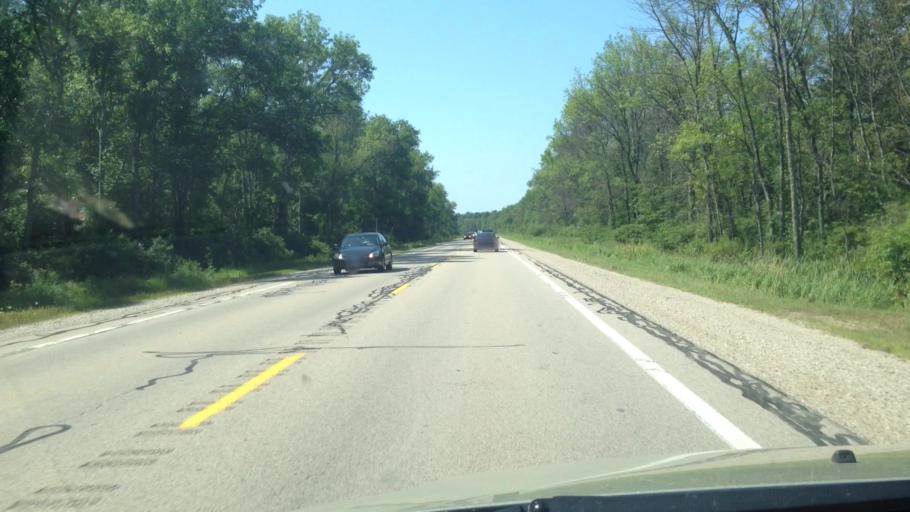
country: US
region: Michigan
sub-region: Menominee County
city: Menominee
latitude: 45.3291
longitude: -87.4242
